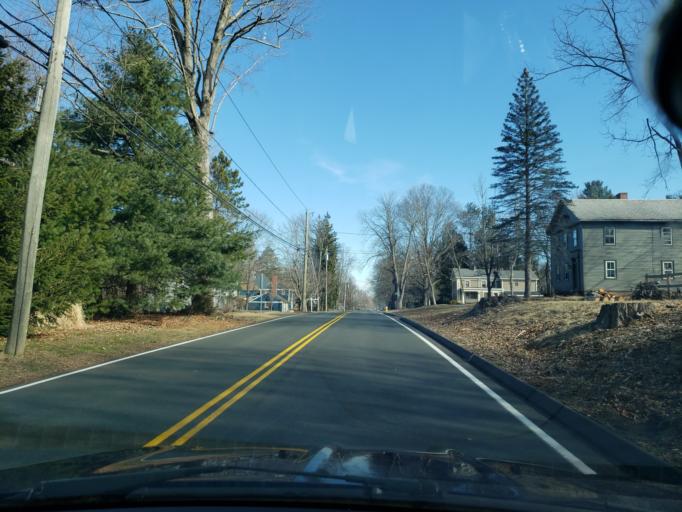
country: US
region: Connecticut
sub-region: Hartford County
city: Suffield Depot
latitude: 41.9694
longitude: -72.6553
